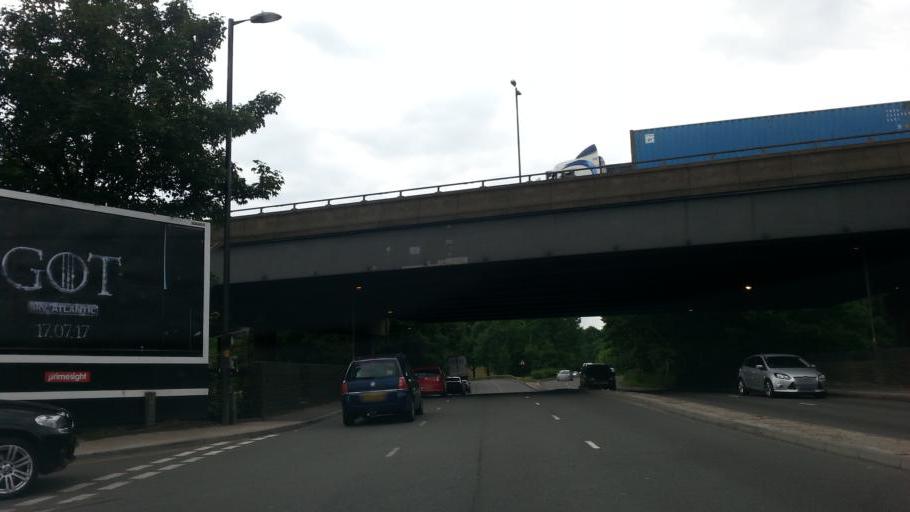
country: GB
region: England
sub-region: Warwickshire
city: Water Orton
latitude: 52.5097
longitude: -1.7967
